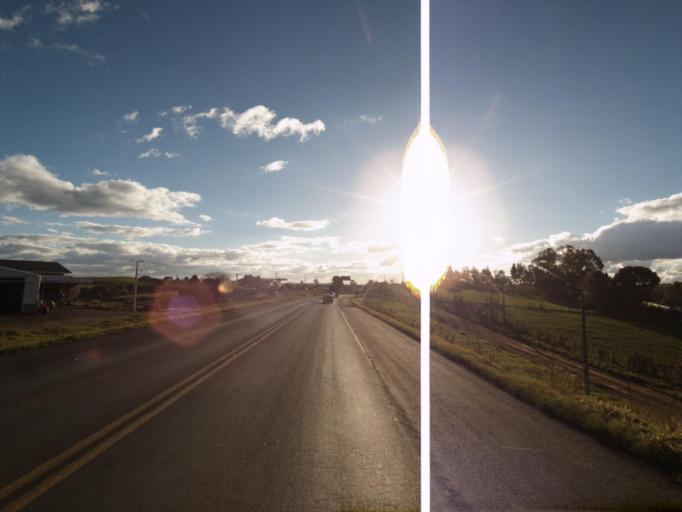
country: BR
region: Santa Catarina
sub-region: Campos Novos
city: Campos Novos
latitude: -27.3883
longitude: -51.2304
